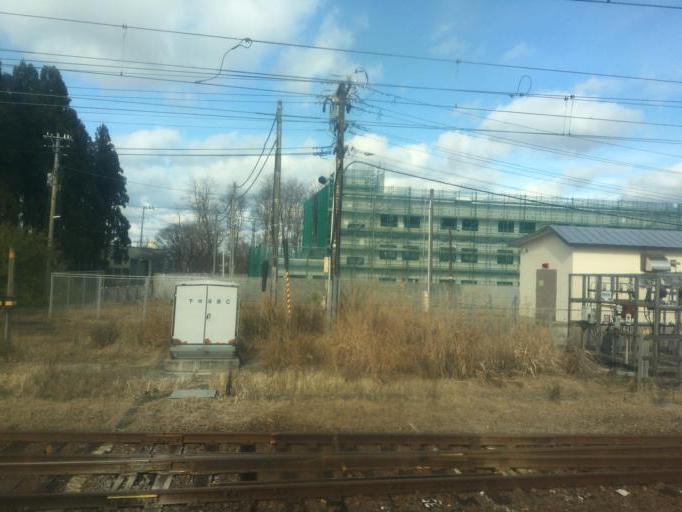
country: JP
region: Akita
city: Noshiromachi
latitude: 40.1906
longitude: 140.0629
